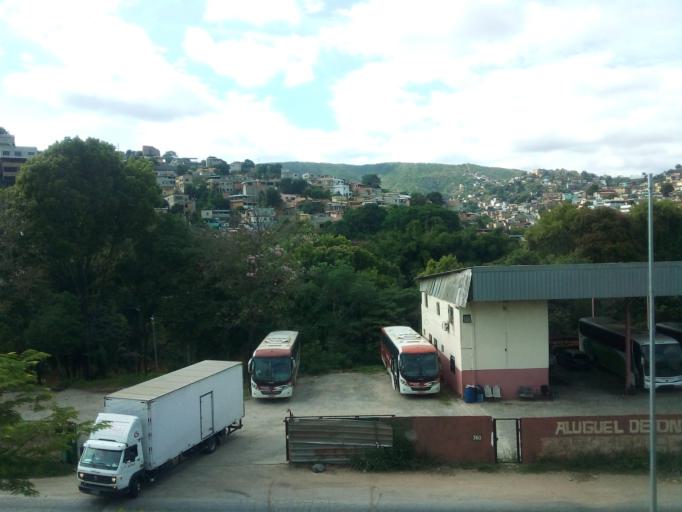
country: BR
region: Minas Gerais
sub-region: Belo Horizonte
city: Belo Horizonte
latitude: -19.8754
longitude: -43.8557
